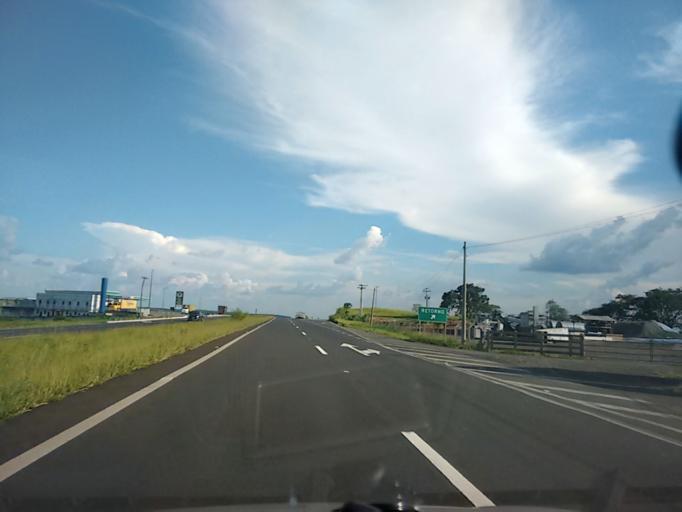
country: BR
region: Sao Paulo
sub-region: Duartina
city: Duartina
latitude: -22.3096
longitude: -49.4950
